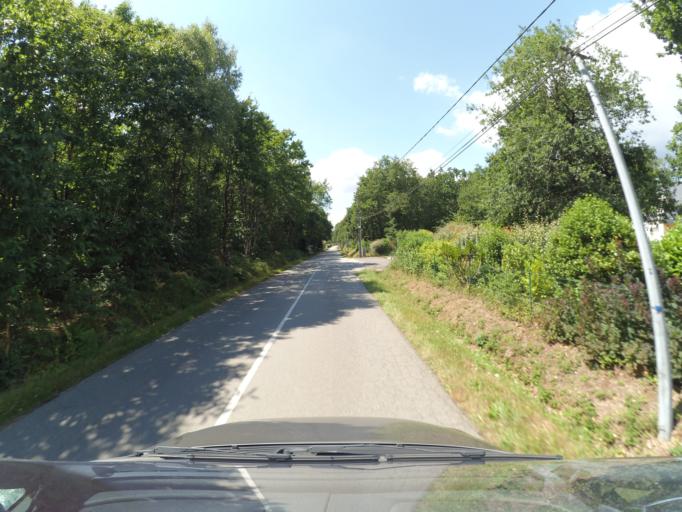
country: FR
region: Brittany
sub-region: Departement du Morbihan
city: Brech
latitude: 47.7303
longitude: -3.0383
